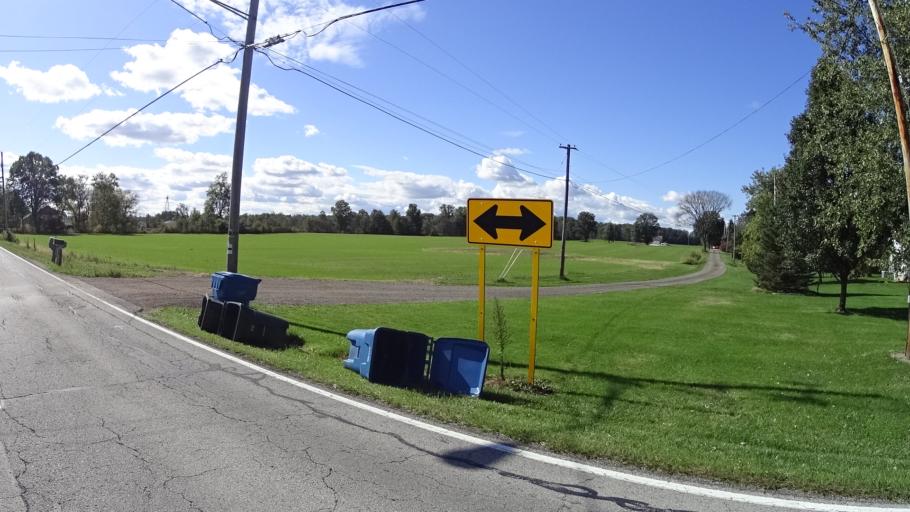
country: US
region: Ohio
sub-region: Lorain County
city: Grafton
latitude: 41.2644
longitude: -82.0803
